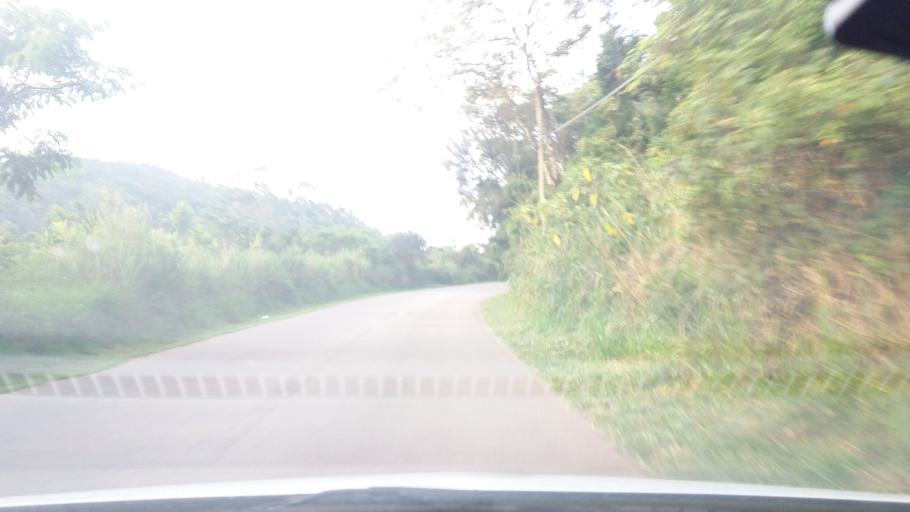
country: BR
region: Sao Paulo
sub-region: Bom Jesus Dos Perdoes
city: Bom Jesus dos Perdoes
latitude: -23.1645
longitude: -46.4774
